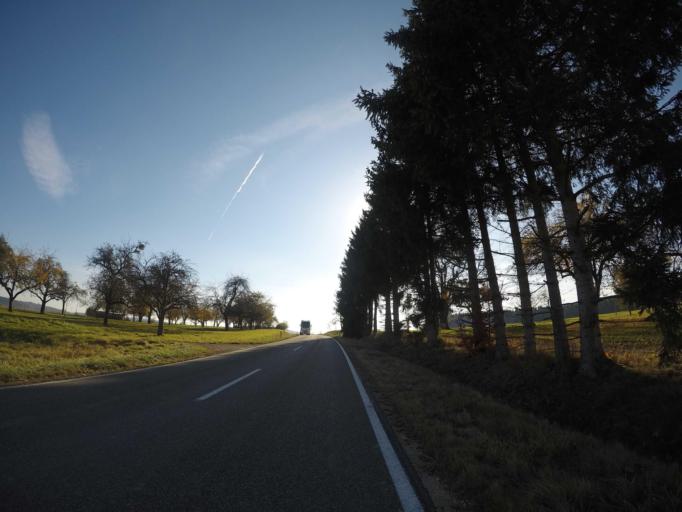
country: DE
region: Baden-Wuerttemberg
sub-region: Tuebingen Region
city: Obermarchtal
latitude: 48.2256
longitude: 9.5647
